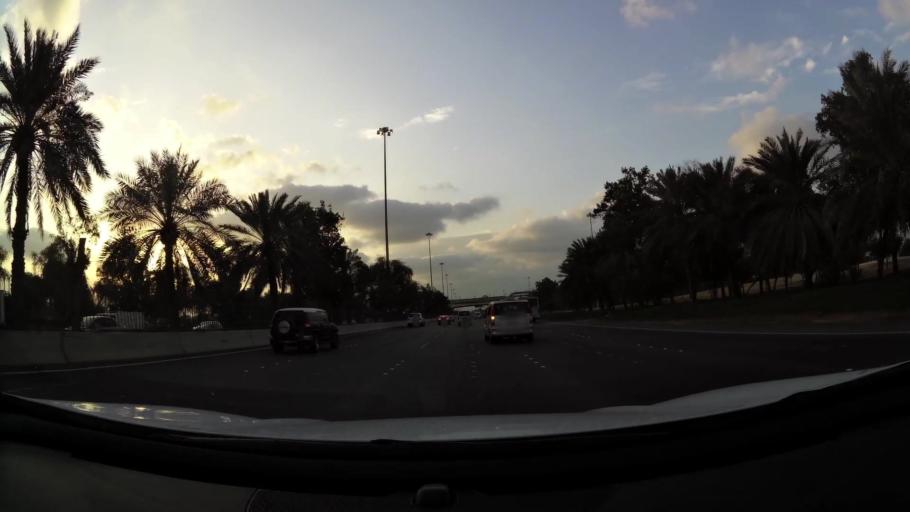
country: AE
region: Abu Dhabi
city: Abu Dhabi
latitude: 24.4135
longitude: 54.5065
